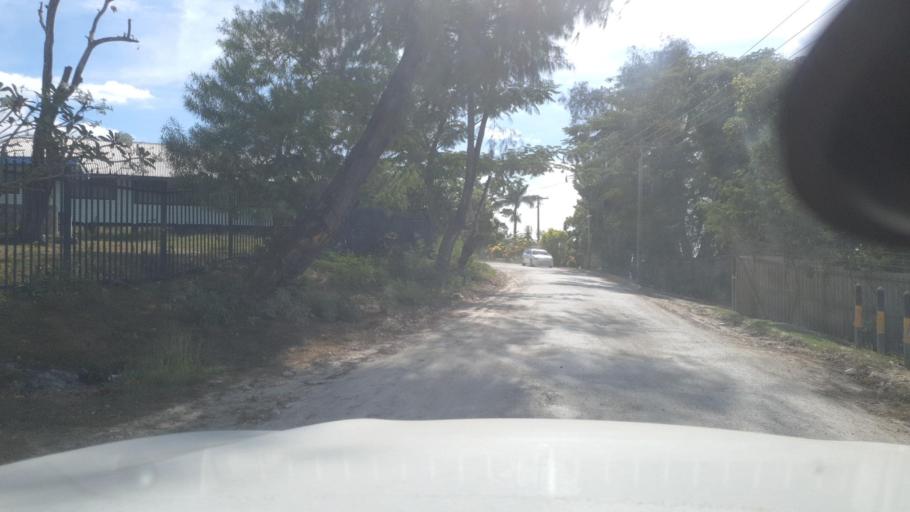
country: SB
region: Guadalcanal
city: Honiara
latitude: -9.4331
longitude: 159.9475
